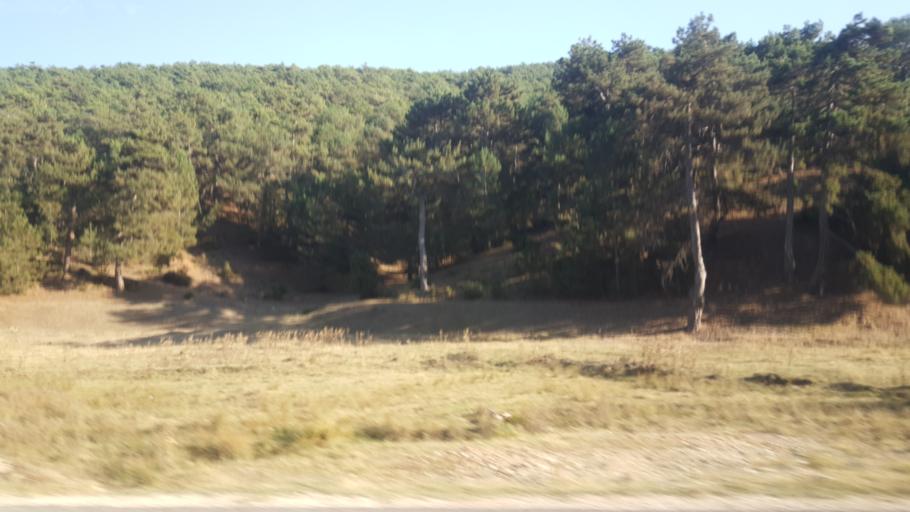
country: TR
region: Eskisehir
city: Kirka
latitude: 39.1065
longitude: 30.5818
